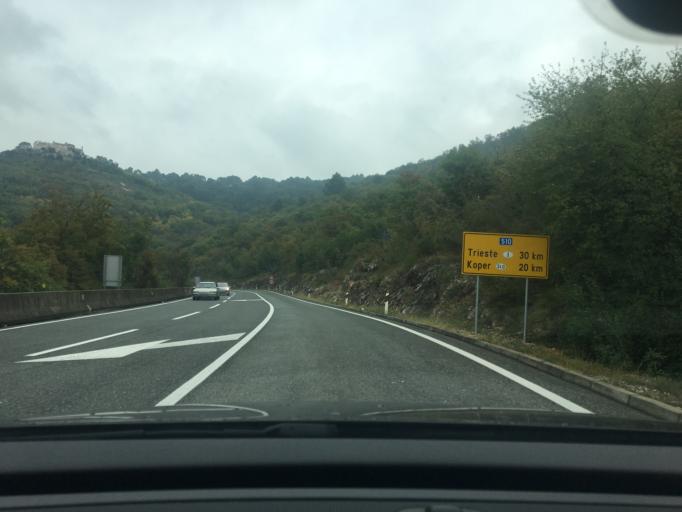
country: HR
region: Istarska
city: Buje
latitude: 45.4532
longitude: 13.6463
